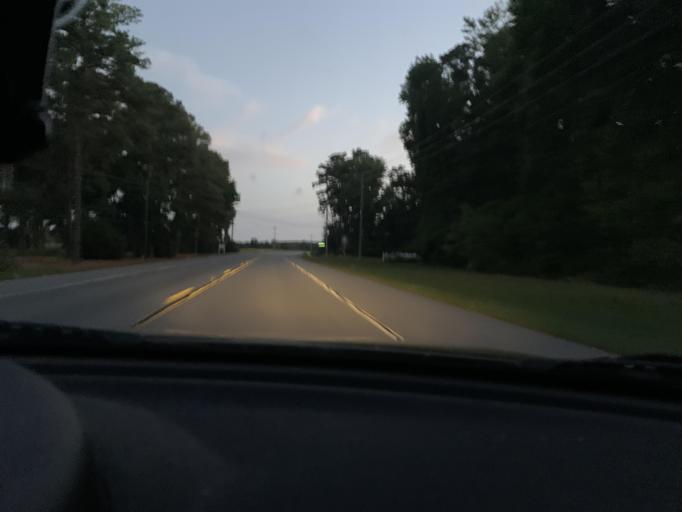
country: US
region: Maryland
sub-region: Talbot County
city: Saint Michaels
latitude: 38.7542
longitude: -76.3206
